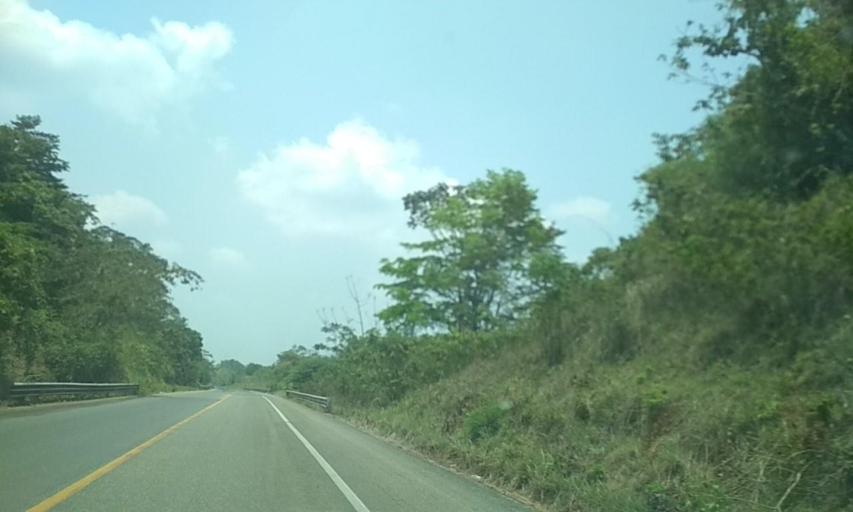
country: MX
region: Tabasco
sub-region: Huimanguillo
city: Francisco Rueda
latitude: 17.6817
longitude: -93.8880
